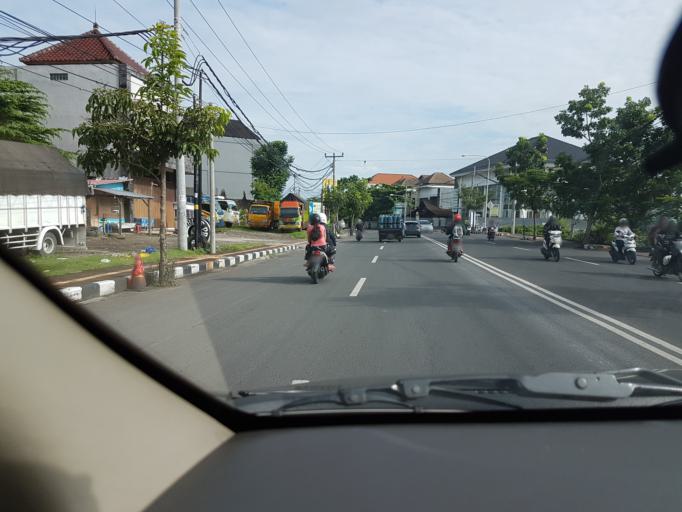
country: ID
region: Bali
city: Denpasar
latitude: -8.6718
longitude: 115.1913
